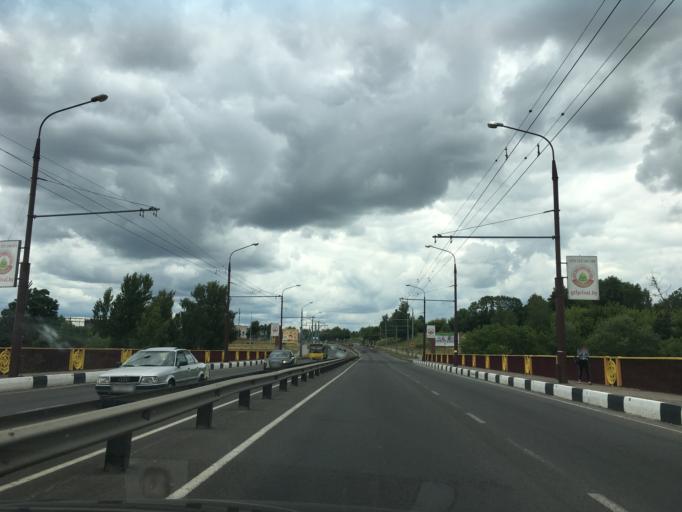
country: BY
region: Grodnenskaya
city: Hrodna
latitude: 53.6615
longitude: 23.8598
